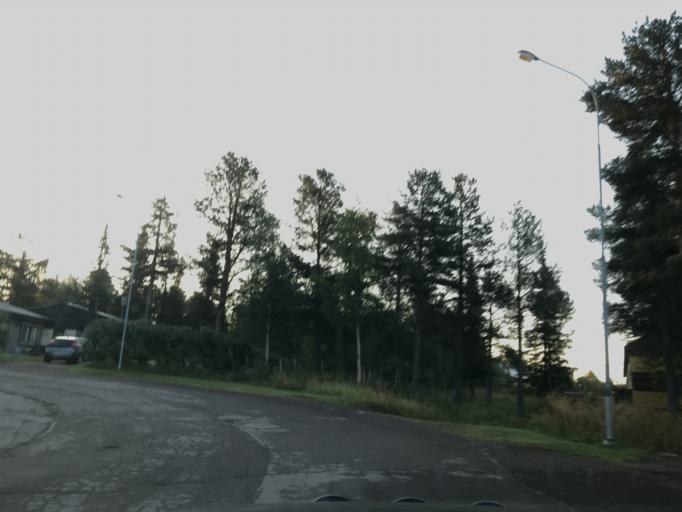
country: SE
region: Norrbotten
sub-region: Gallivare Kommun
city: Malmberget
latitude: 67.6509
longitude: 21.0475
